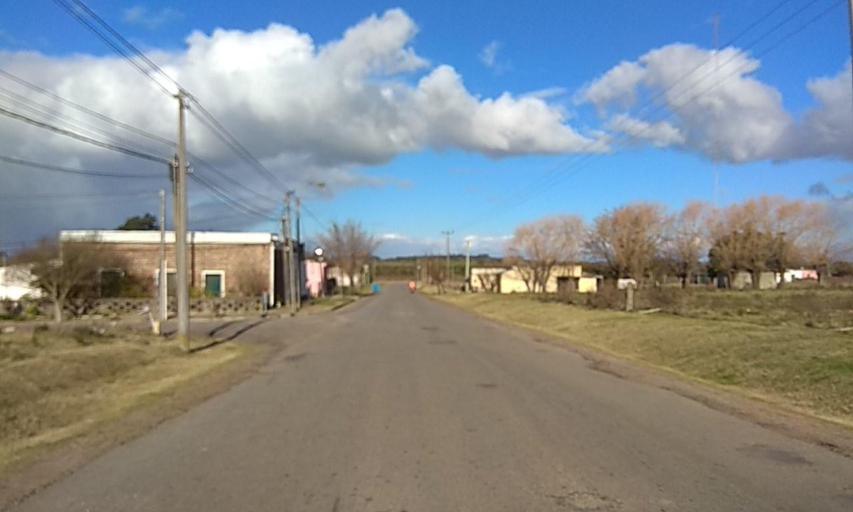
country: UY
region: Florida
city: Florida
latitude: -34.1084
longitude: -56.2228
